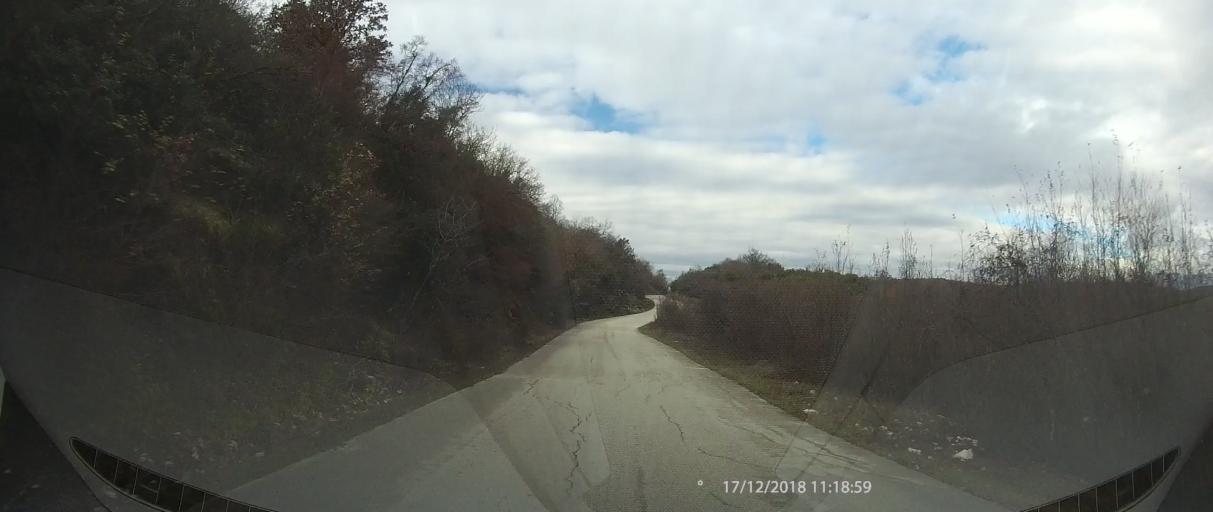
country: GR
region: Epirus
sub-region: Nomos Ioanninon
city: Kalpaki
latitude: 39.9563
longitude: 20.6532
